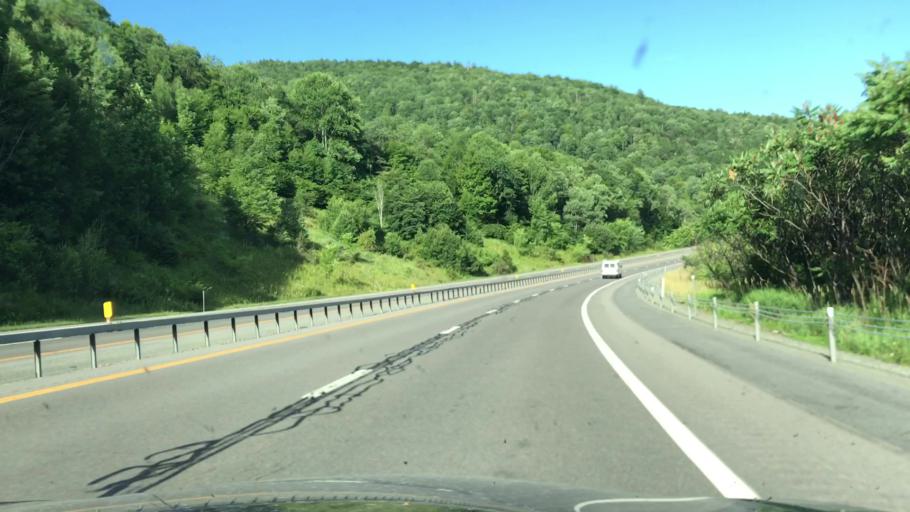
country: US
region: New York
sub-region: Delaware County
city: Hancock
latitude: 41.9761
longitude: -75.1997
